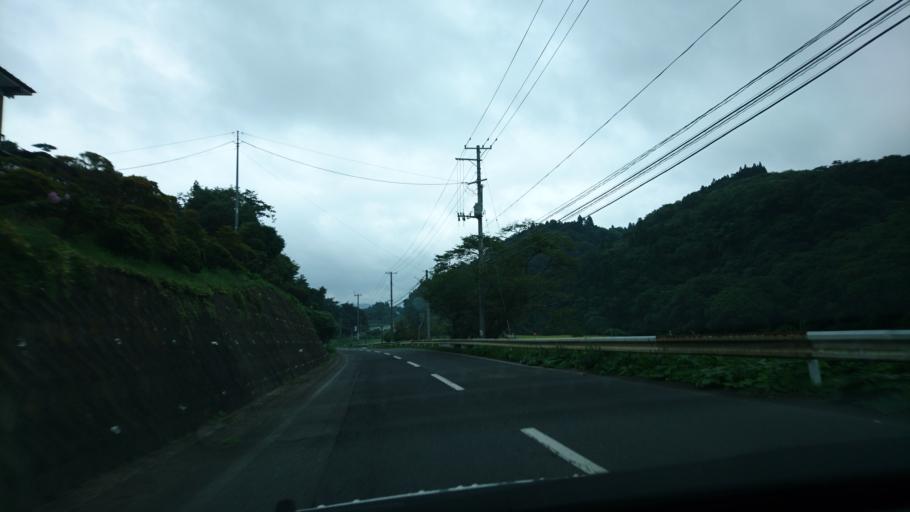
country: JP
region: Iwate
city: Ichinoseki
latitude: 38.9142
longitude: 141.0798
